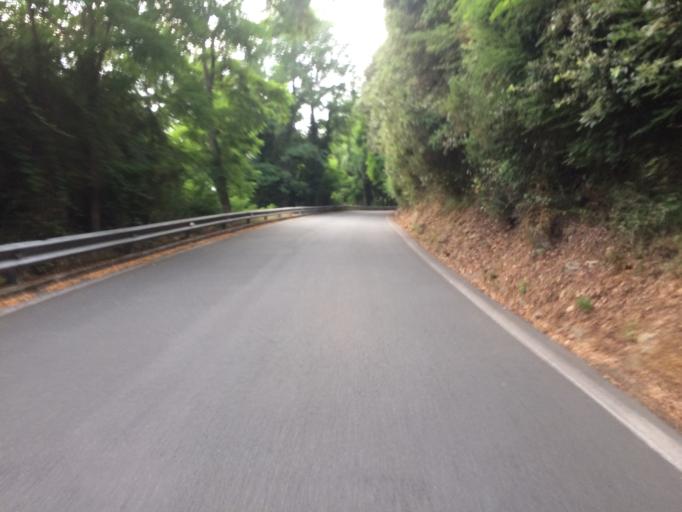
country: IT
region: Liguria
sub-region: Provincia di Imperia
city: Seborga
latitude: 43.8461
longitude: 7.7391
